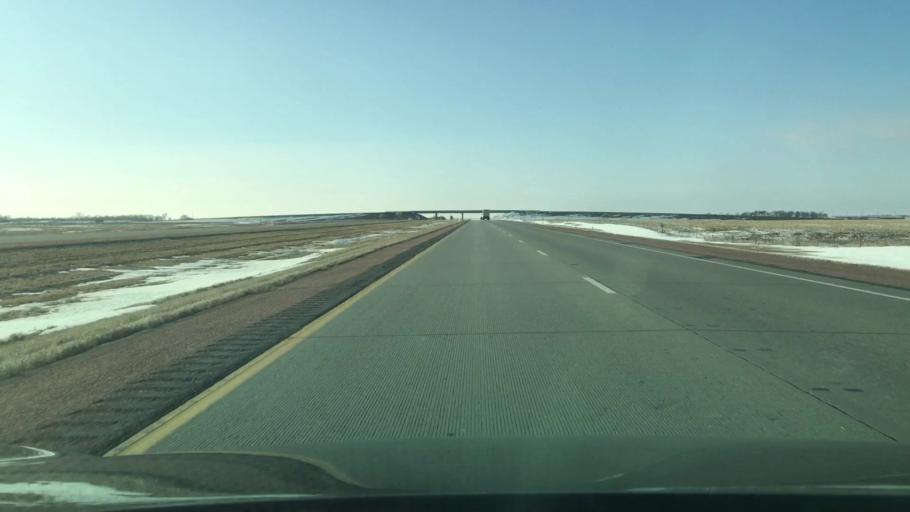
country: US
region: South Dakota
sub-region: Aurora County
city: Plankinton
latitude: 43.7075
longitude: -98.5173
